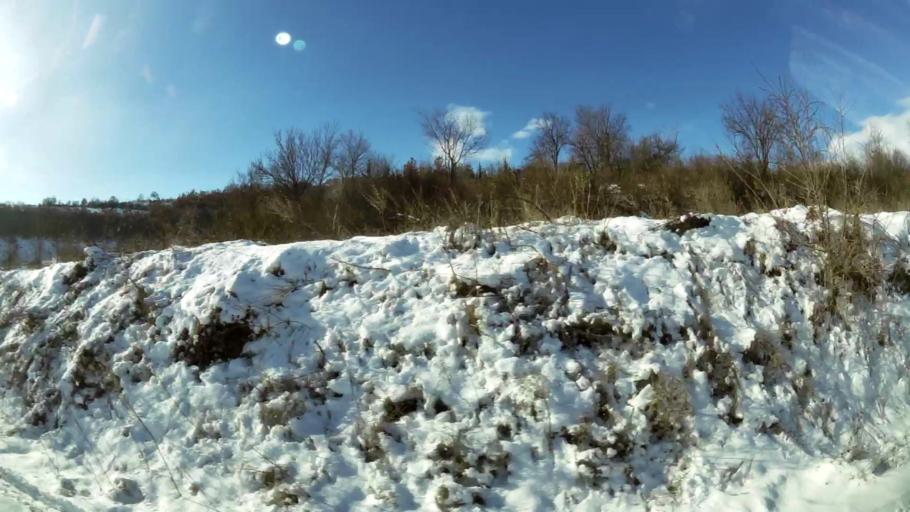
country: MK
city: Ljubin
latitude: 41.9832
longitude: 21.2993
